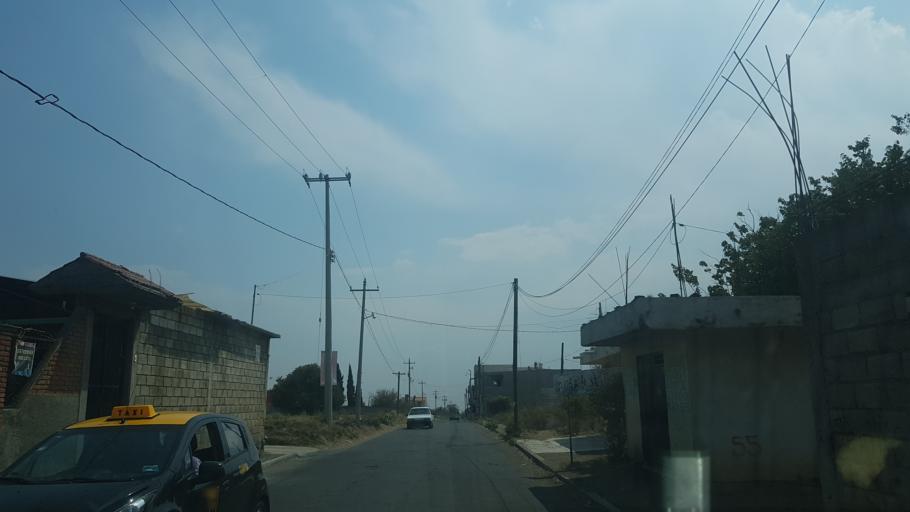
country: MX
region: Puebla
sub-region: Tianguismanalco
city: San Martin Tlapala
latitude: 18.9748
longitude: -98.4524
